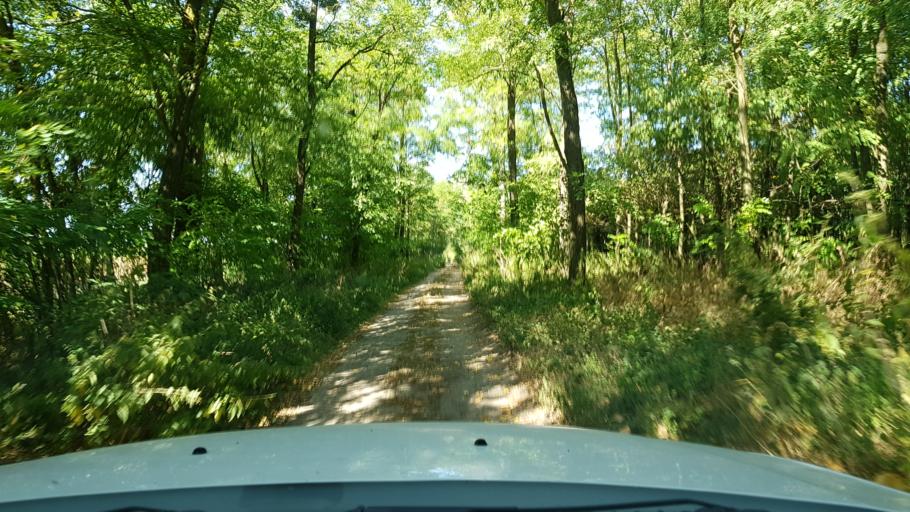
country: PL
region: West Pomeranian Voivodeship
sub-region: Powiat gryfinski
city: Cedynia
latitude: 52.8532
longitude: 14.2269
